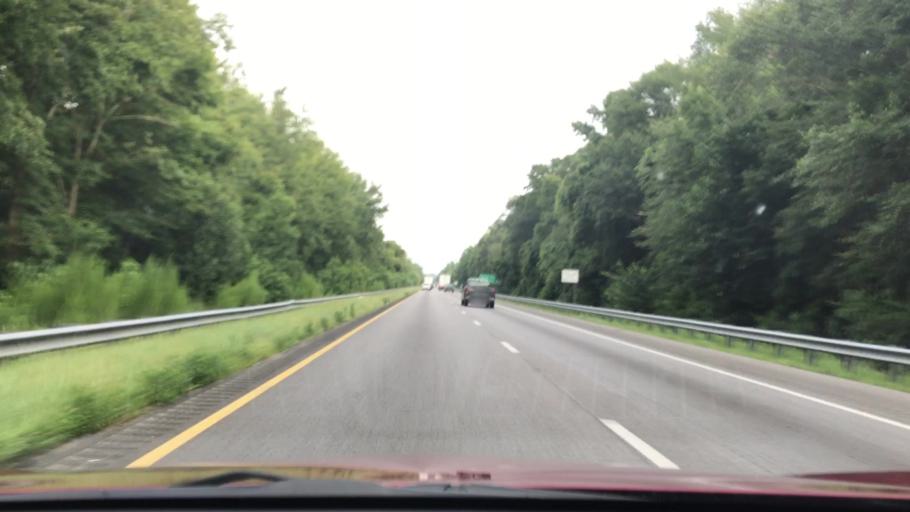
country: US
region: South Carolina
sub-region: Dorchester County
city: Ridgeville
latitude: 33.1446
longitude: -80.3254
